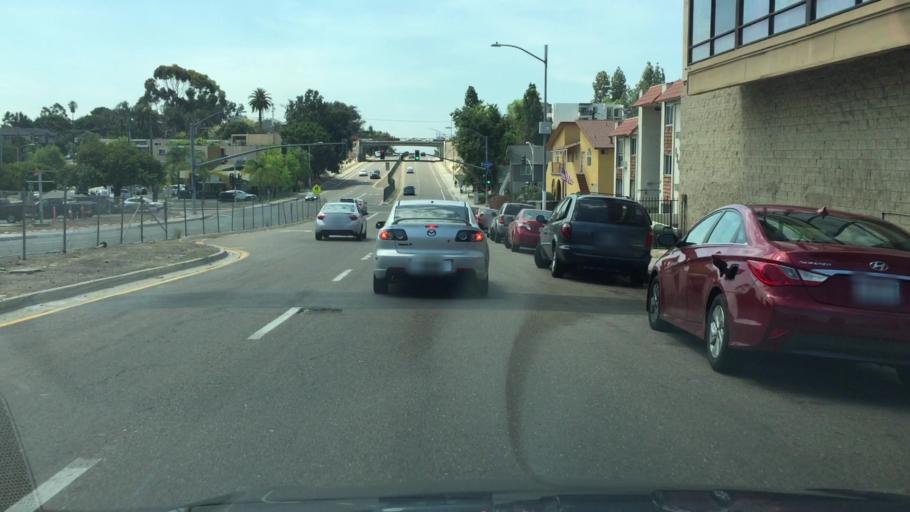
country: US
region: California
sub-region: San Diego County
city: Lemon Grove
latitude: 32.7559
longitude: -117.0795
